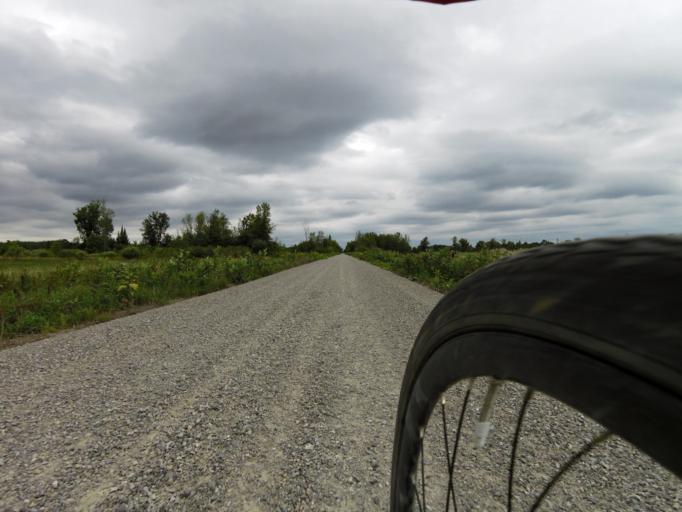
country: CA
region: Ontario
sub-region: Lanark County
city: Smiths Falls
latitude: 44.9258
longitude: -76.0319
